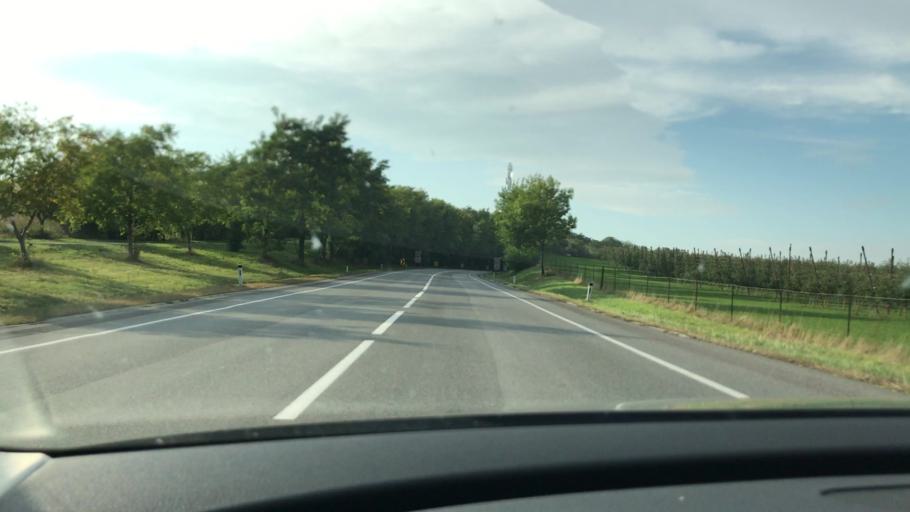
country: AT
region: Lower Austria
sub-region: Politischer Bezirk Mistelbach
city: Drasenhofen
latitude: 48.7449
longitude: 16.6539
